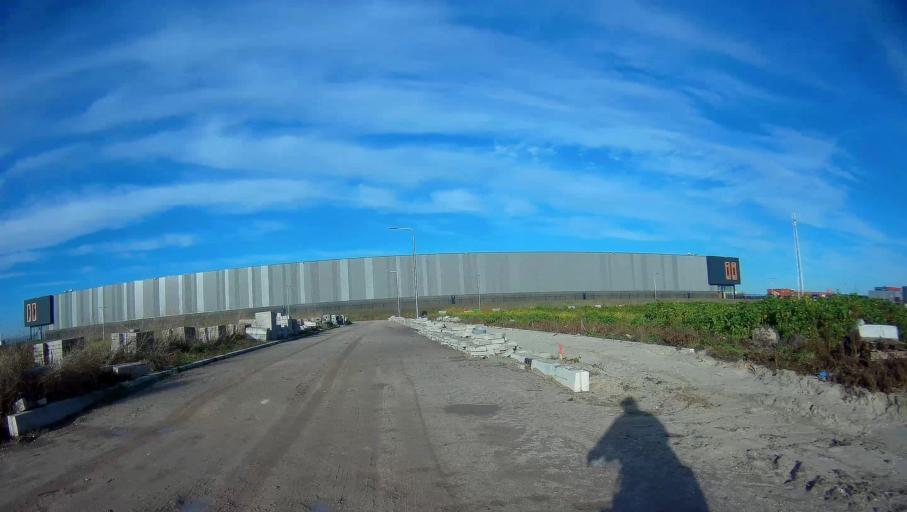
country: NL
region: South Holland
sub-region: Gemeente Lansingerland
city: Berkel en Rodenrijs
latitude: 51.9758
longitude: 4.4419
